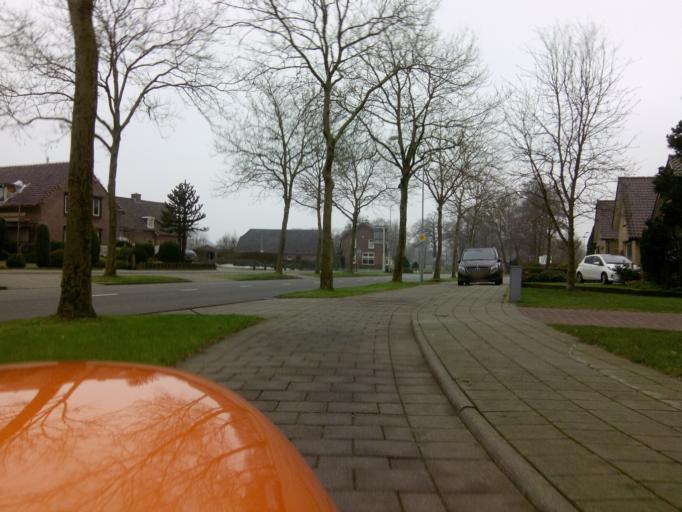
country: NL
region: Gelderland
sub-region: Gemeente Barneveld
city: Voorthuizen
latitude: 52.1909
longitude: 5.6042
